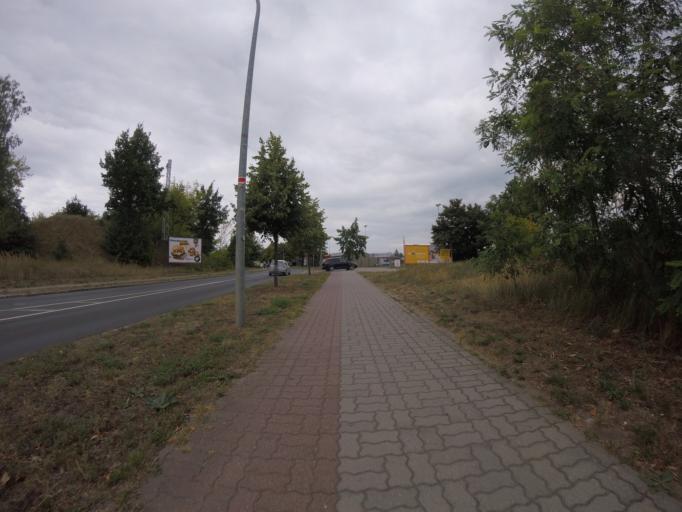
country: DE
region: Brandenburg
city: Oranienburg
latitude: 52.7472
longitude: 13.2565
